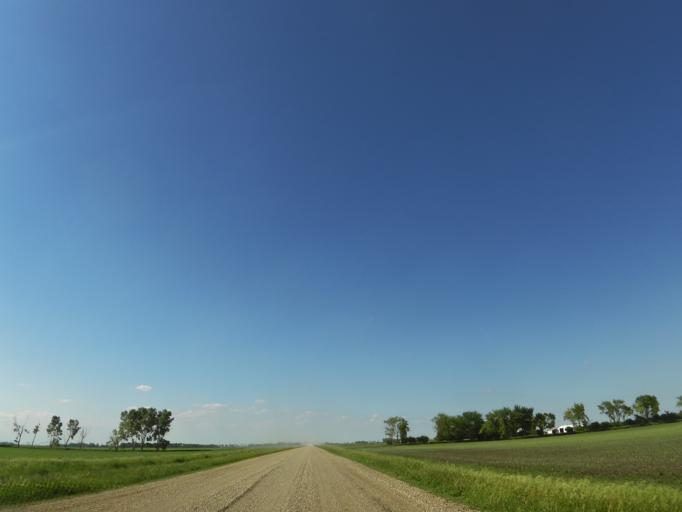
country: US
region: North Dakota
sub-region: Walsh County
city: Grafton
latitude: 48.3296
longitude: -97.2555
